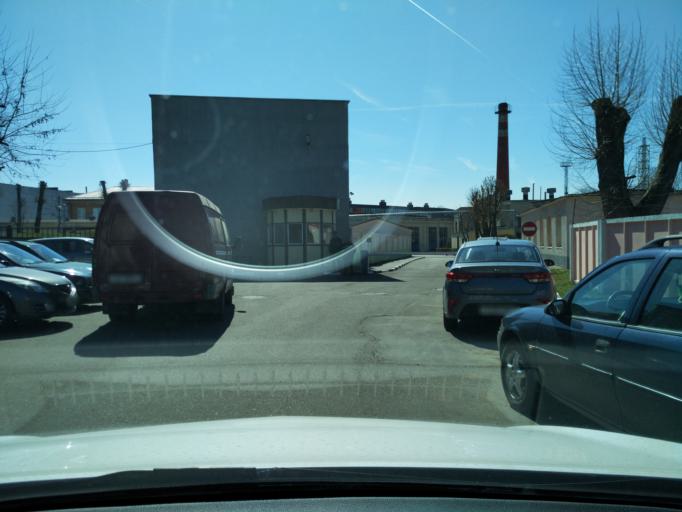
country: BY
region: Minsk
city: Minsk
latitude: 53.8780
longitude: 27.5266
